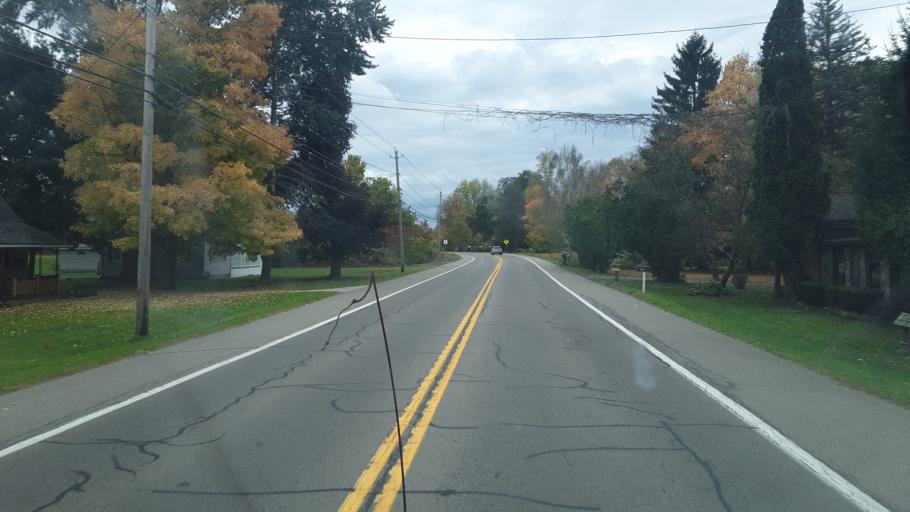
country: US
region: New York
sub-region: Allegany County
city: Belmont
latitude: 42.2154
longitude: -78.0212
